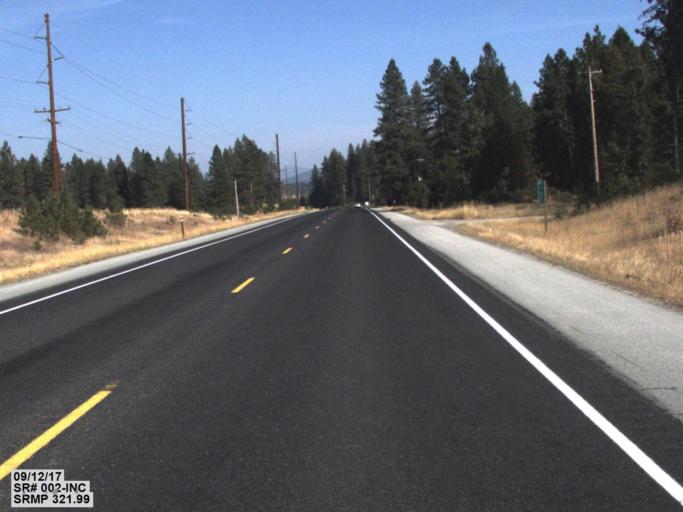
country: US
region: Washington
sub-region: Pend Oreille County
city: Newport
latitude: 48.0973
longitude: -117.2657
